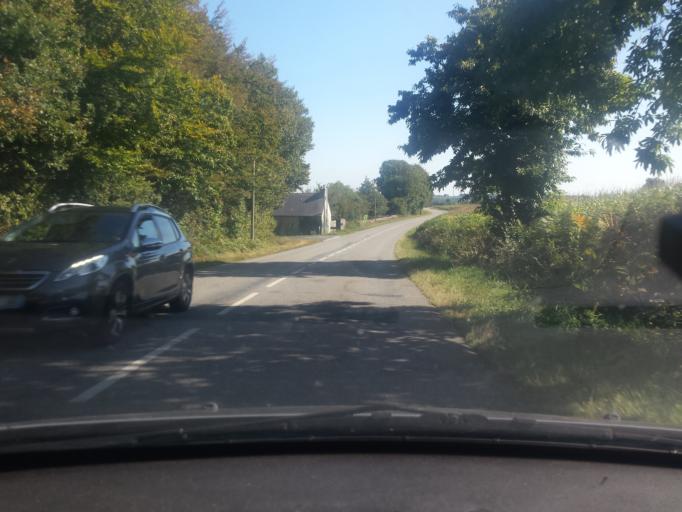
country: FR
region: Brittany
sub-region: Departement du Morbihan
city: Cleguerec
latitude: 48.1319
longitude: -3.1449
